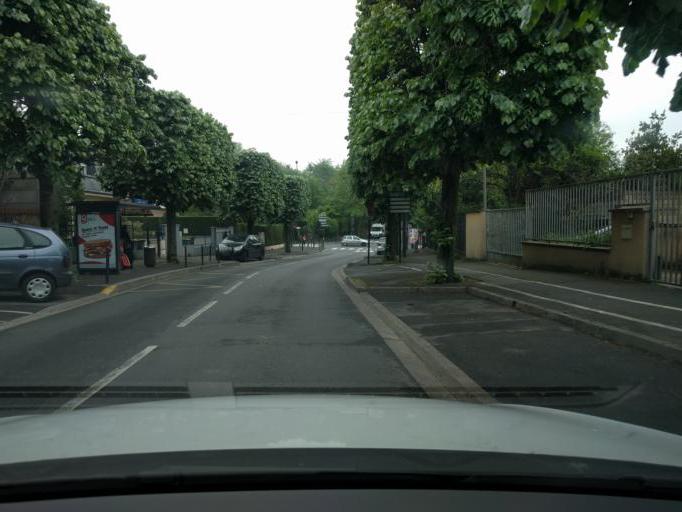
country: FR
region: Ile-de-France
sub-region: Departement du Val-de-Marne
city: Vitry-sur-Seine
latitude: 48.7985
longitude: 2.3914
